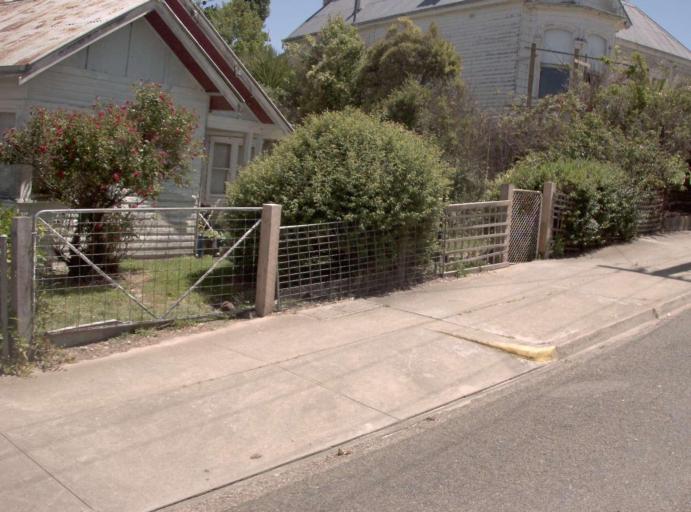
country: AU
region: Victoria
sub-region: Alpine
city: Mount Beauty
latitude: -37.0994
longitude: 147.5933
